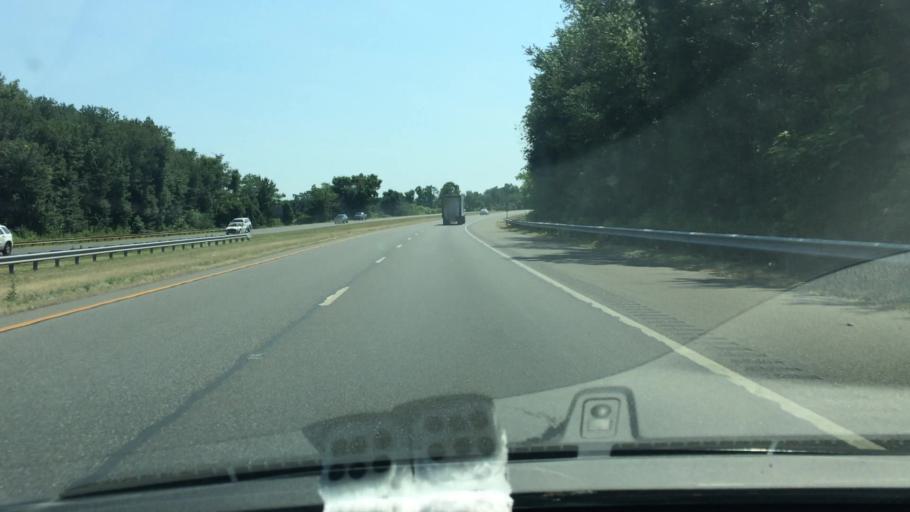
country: US
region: New Jersey
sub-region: Gloucester County
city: Gibbstown
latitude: 39.7993
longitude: -75.3163
